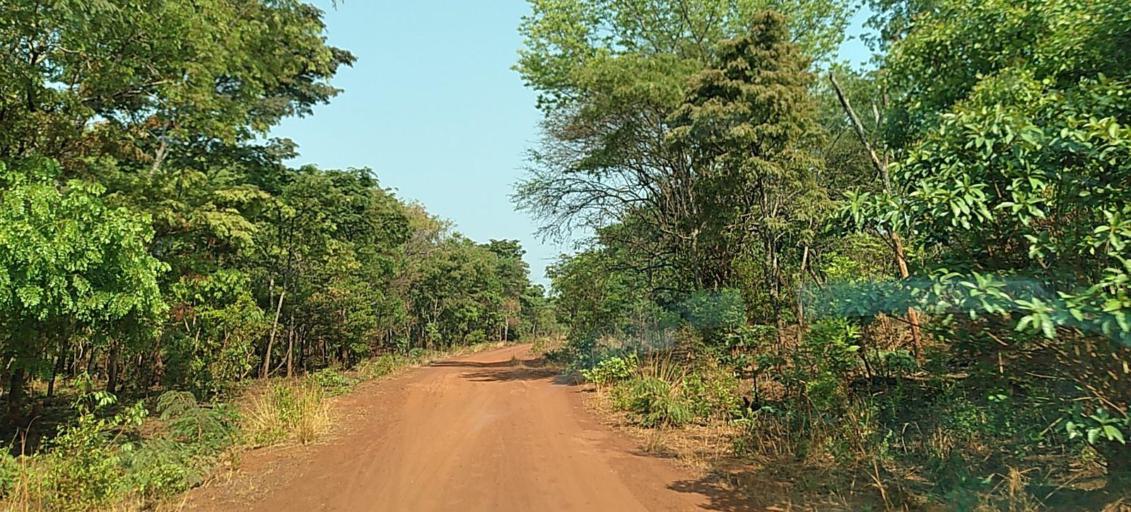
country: ZM
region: Copperbelt
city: Chingola
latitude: -12.8852
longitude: 27.4136
